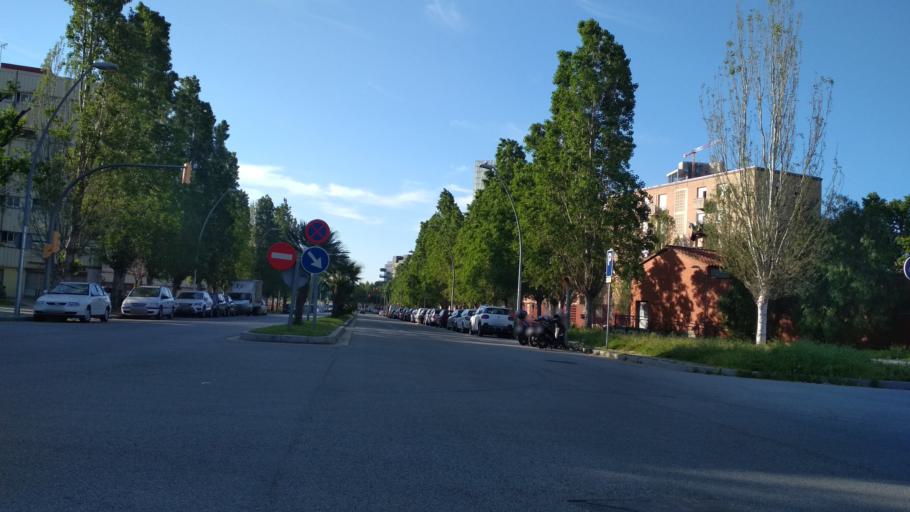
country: ES
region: Catalonia
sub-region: Provincia de Barcelona
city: Sant Adria de Besos
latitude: 41.4168
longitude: 2.2185
